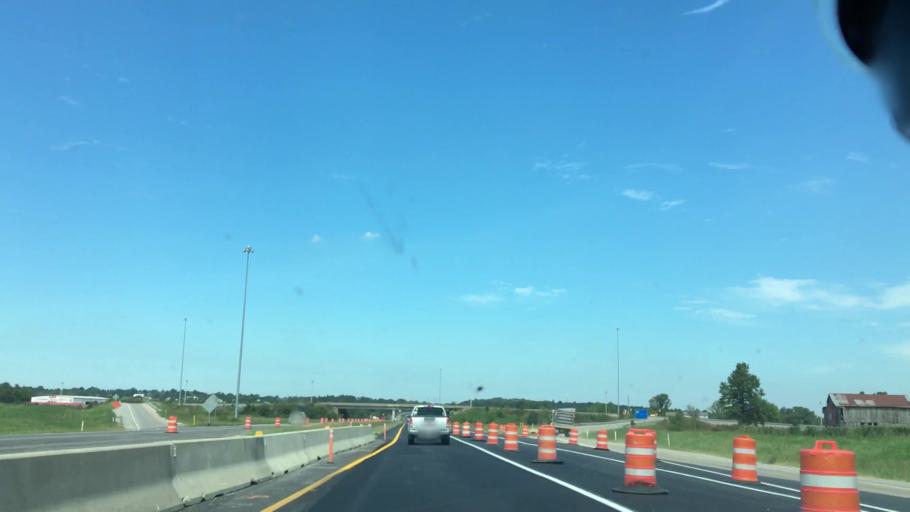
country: US
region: Kentucky
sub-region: Hopkins County
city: Nortonville
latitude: 37.0467
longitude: -87.4633
